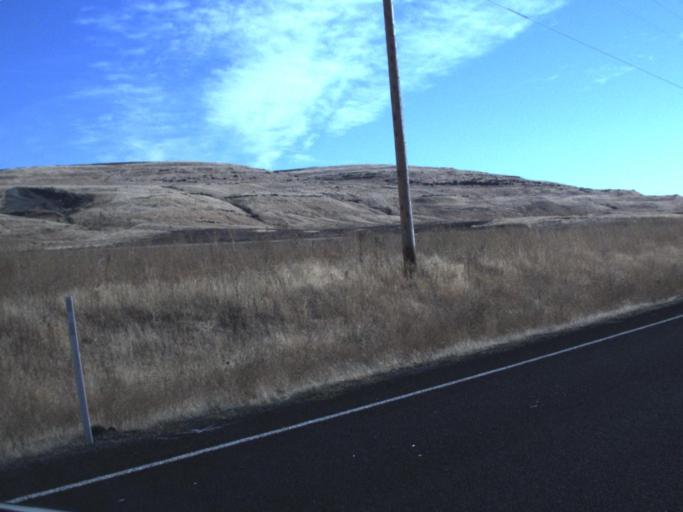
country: US
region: Washington
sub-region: Franklin County
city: Connell
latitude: 46.6488
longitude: -118.5937
